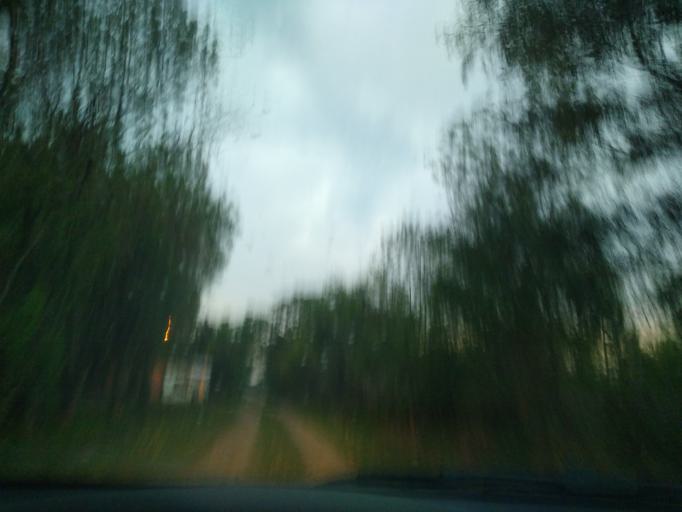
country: AR
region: Chaco
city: Puerto Tirol
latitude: -27.3755
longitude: -59.0834
